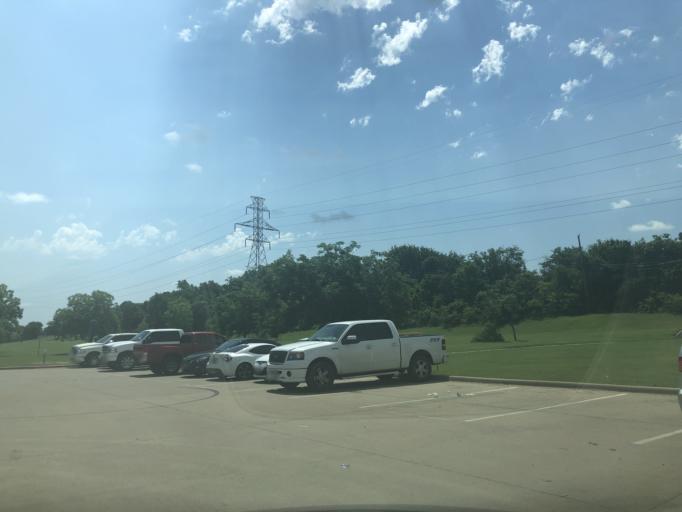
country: US
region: Texas
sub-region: Dallas County
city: Grand Prairie
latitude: 32.7249
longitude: -97.0129
